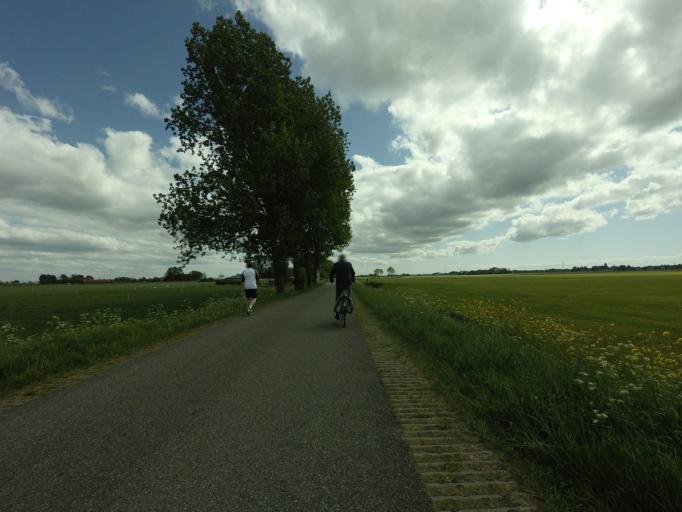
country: NL
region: Friesland
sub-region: Sudwest Fryslan
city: Bolsward
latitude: 53.0811
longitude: 5.5510
